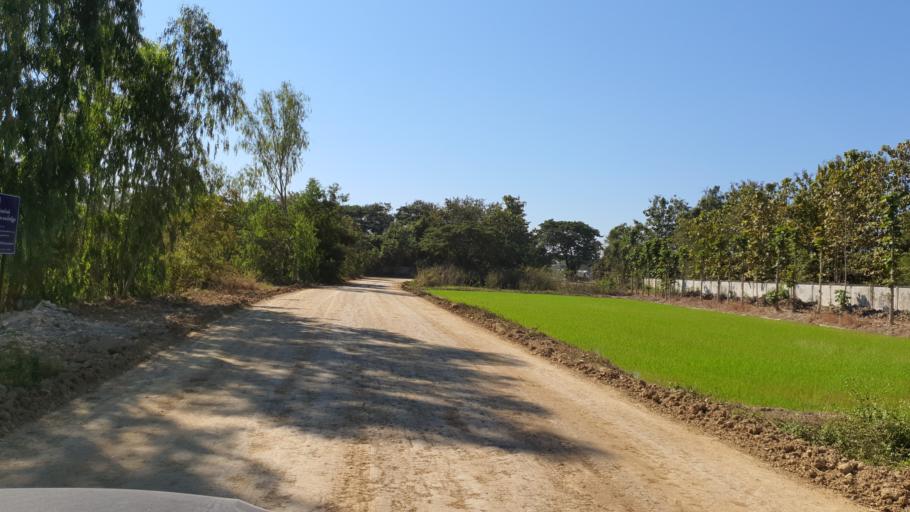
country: TH
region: Lamphun
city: Ban Thi
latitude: 18.6641
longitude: 99.1053
